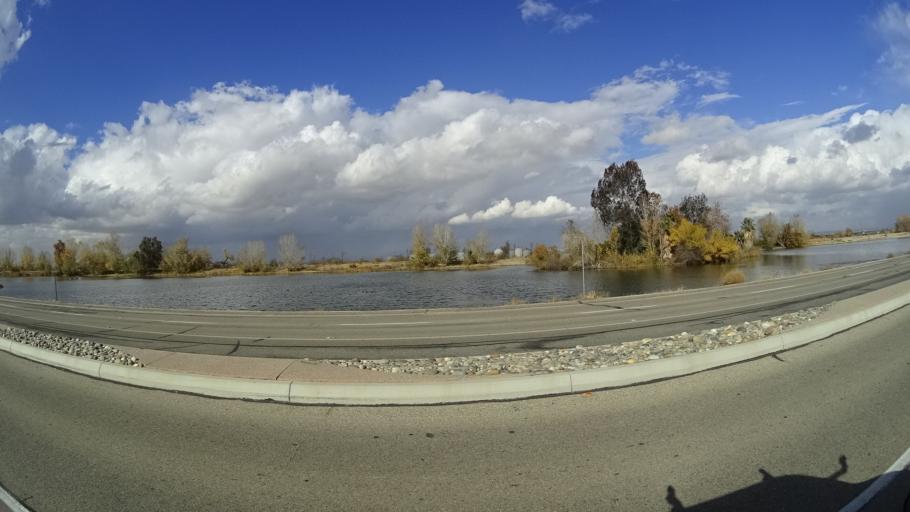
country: US
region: California
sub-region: Kern County
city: Greenacres
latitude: 35.3619
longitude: -119.0742
